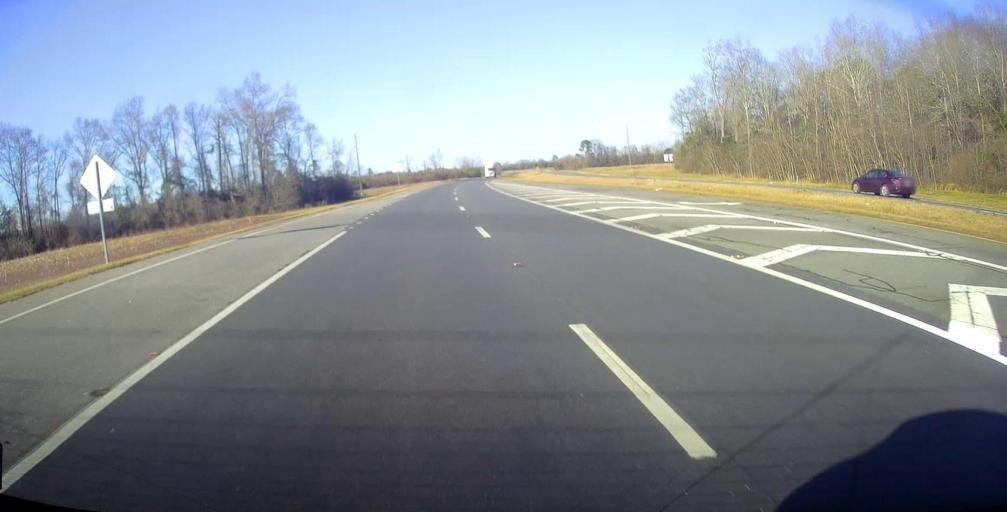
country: US
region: Georgia
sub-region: Sumter County
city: Americus
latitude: 31.9032
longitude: -84.2626
